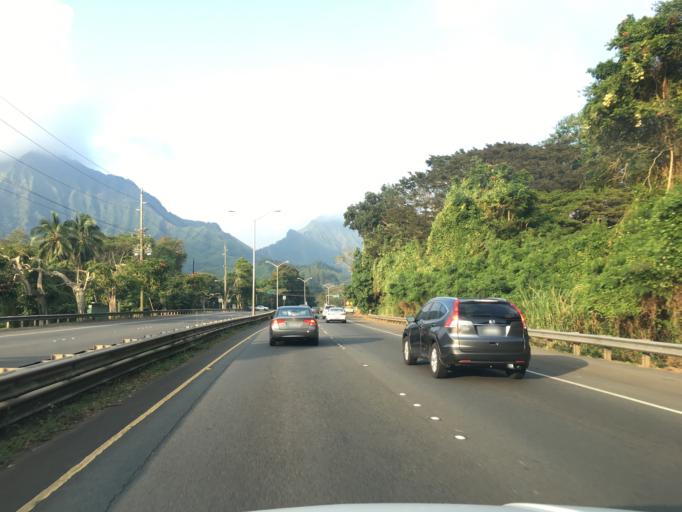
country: US
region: Hawaii
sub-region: Honolulu County
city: Maunawili
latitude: 21.3774
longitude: -157.7615
